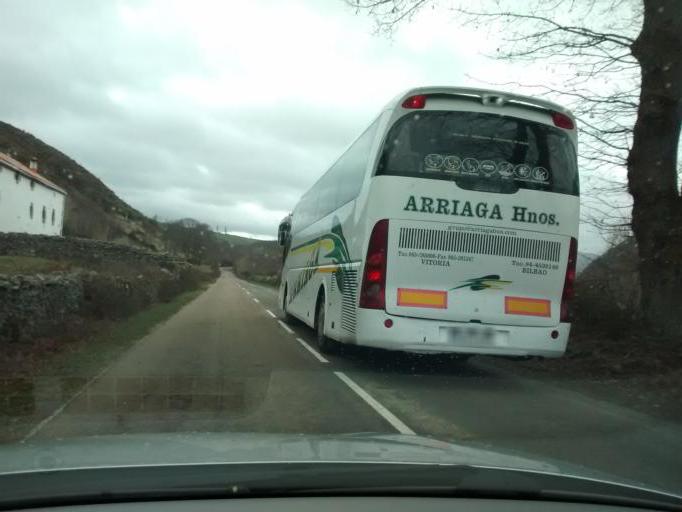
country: ES
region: Castille and Leon
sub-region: Provincia de Burgos
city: Espinosa de los Monteros
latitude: 43.0931
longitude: -3.5616
